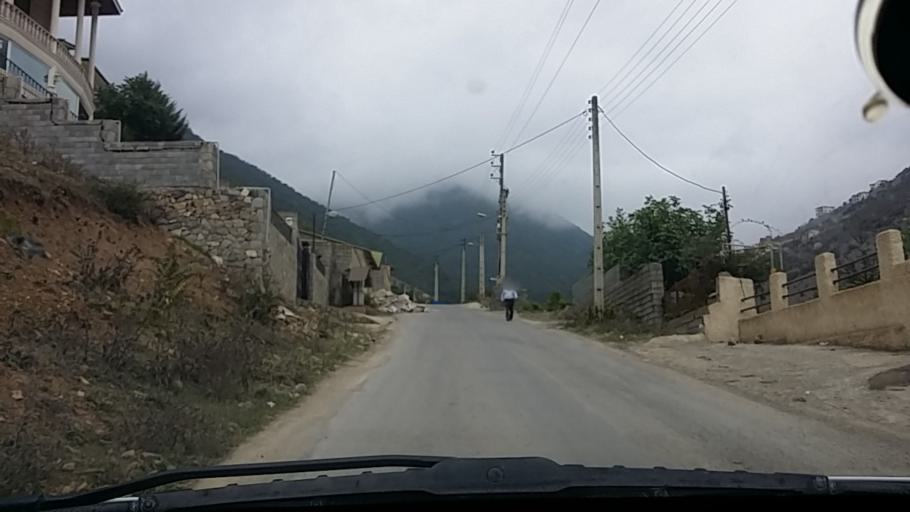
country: IR
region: Mazandaran
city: `Abbasabad
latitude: 36.4758
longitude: 51.1400
